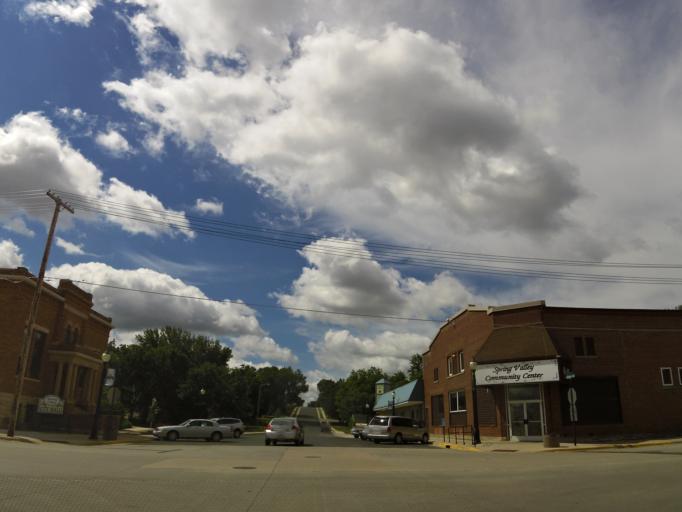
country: US
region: Minnesota
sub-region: Fillmore County
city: Spring Valley
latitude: 43.6871
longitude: -92.3910
